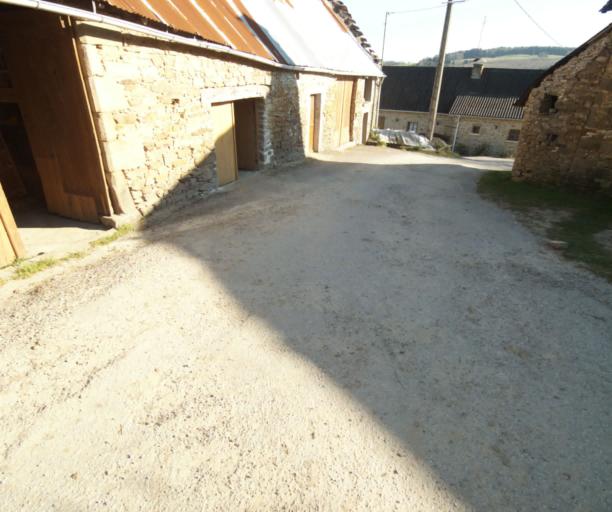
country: FR
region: Limousin
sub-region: Departement de la Correze
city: Chamboulive
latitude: 45.4977
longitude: 1.7266
